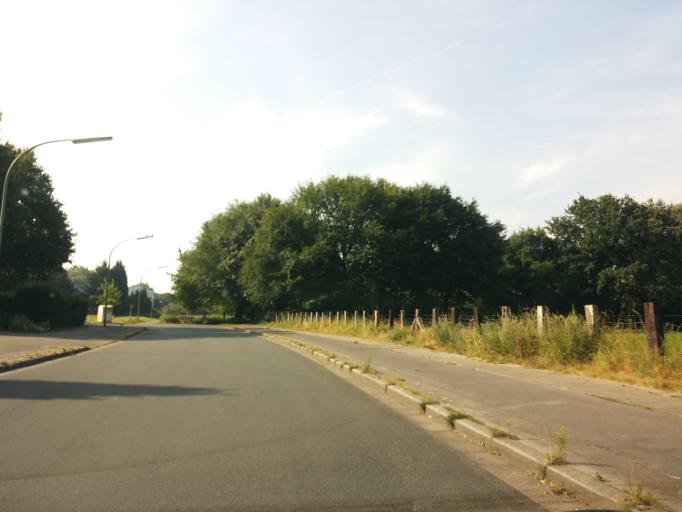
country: DE
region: North Rhine-Westphalia
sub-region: Regierungsbezirk Munster
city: Gladbeck
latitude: 51.5909
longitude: 7.0174
